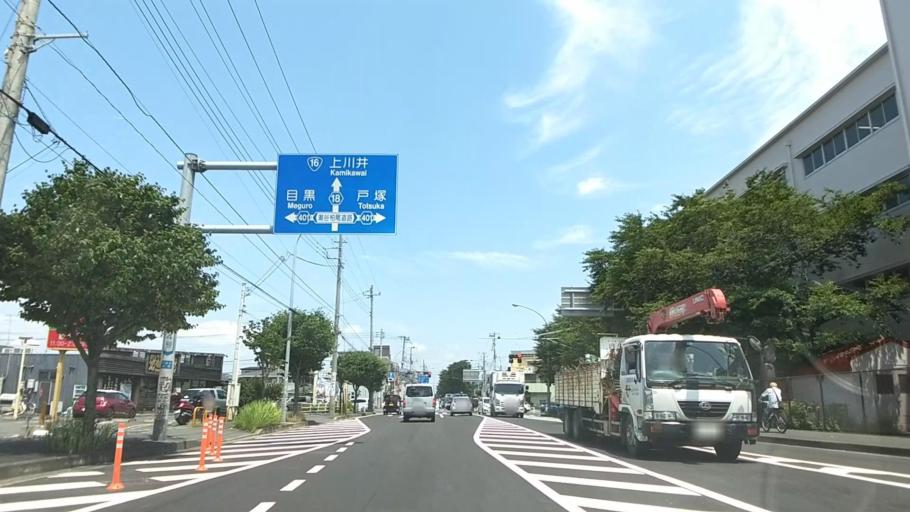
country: JP
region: Kanagawa
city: Minami-rinkan
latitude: 35.4717
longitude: 139.4807
